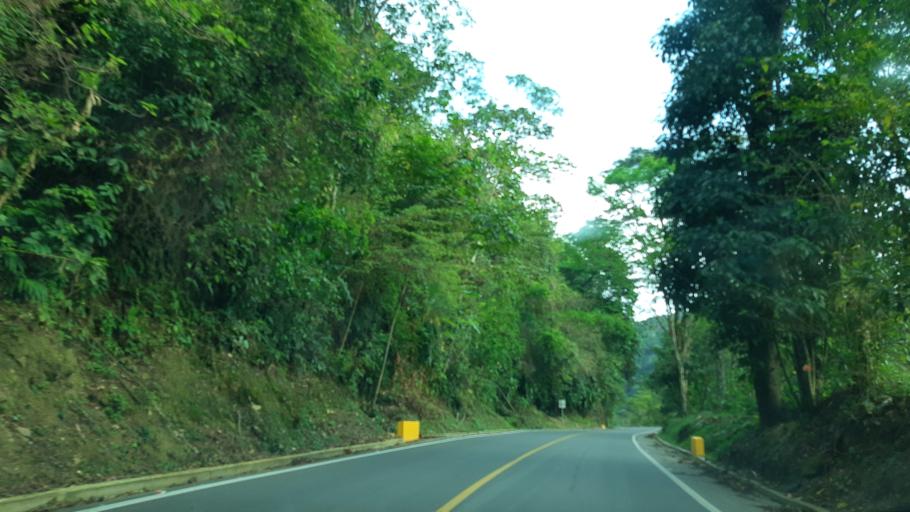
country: CO
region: Boyaca
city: San Luis de Gaceno
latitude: 4.8377
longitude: -73.2140
